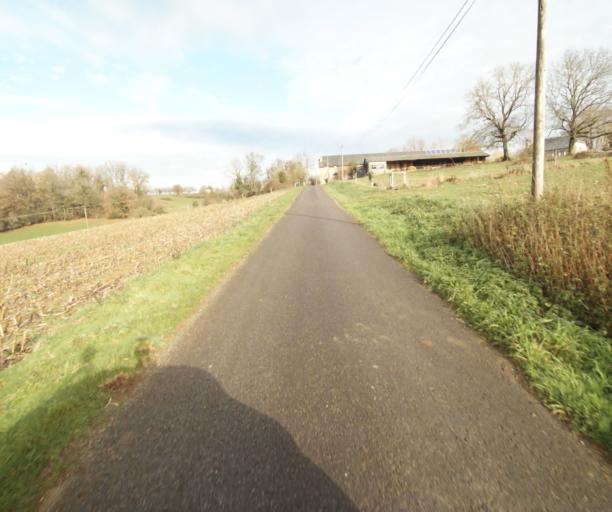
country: FR
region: Limousin
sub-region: Departement de la Correze
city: Saint-Mexant
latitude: 45.2788
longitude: 1.5978
